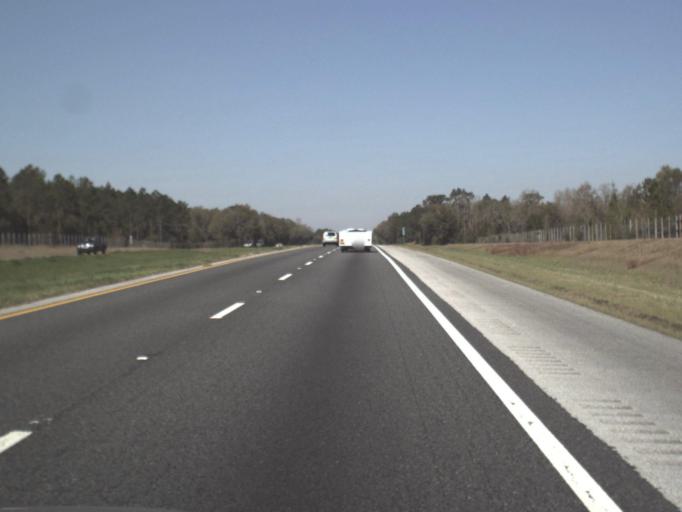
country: US
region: Florida
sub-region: Jackson County
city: Marianna
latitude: 30.6933
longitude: -85.1223
